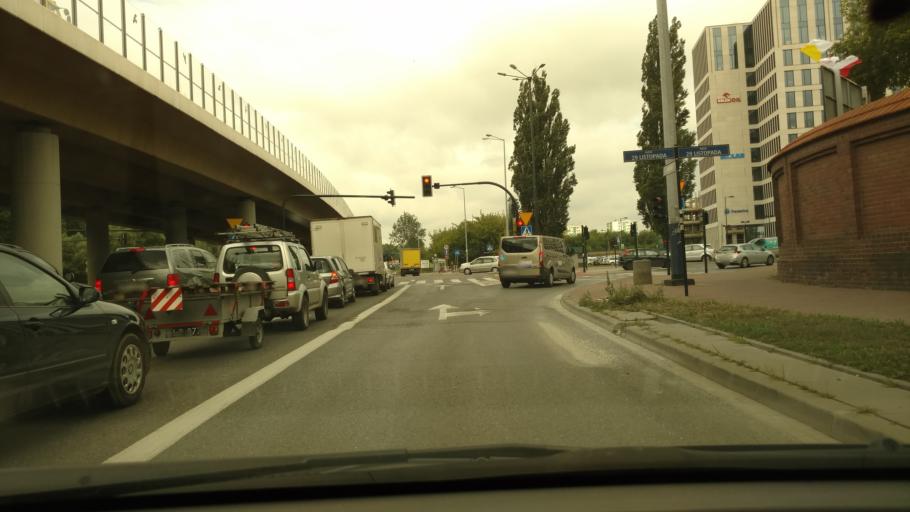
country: PL
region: Lesser Poland Voivodeship
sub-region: Krakow
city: Krakow
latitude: 50.0861
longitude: 19.9556
